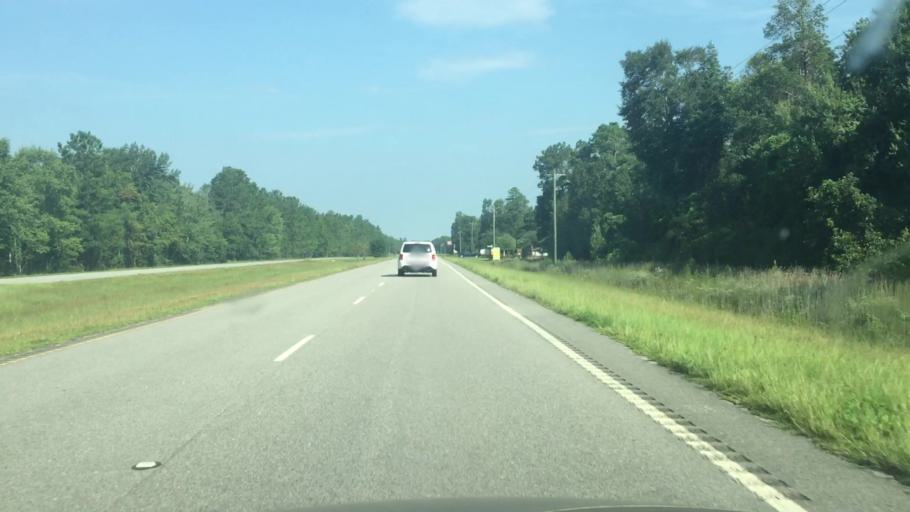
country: US
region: South Carolina
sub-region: Horry County
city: Loris
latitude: 34.0533
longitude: -78.8400
